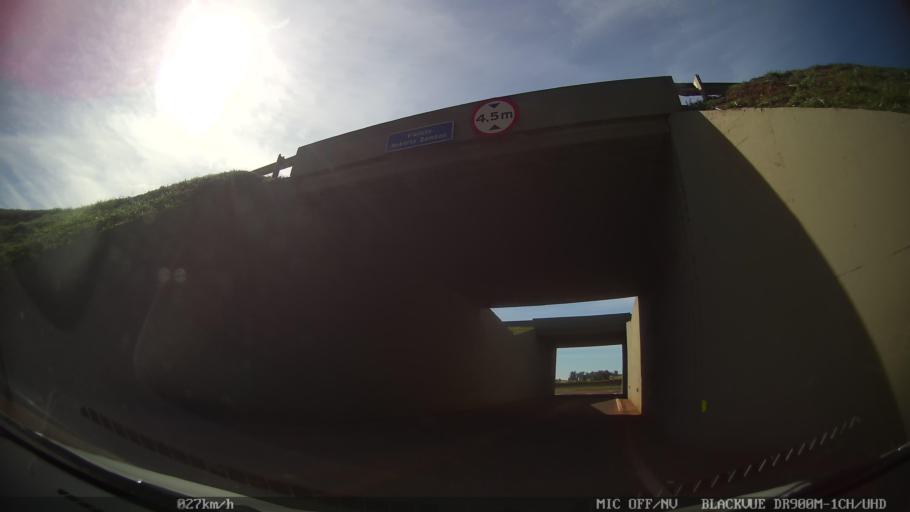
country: BR
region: Sao Paulo
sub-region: Araras
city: Araras
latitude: -22.2741
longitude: -47.3928
